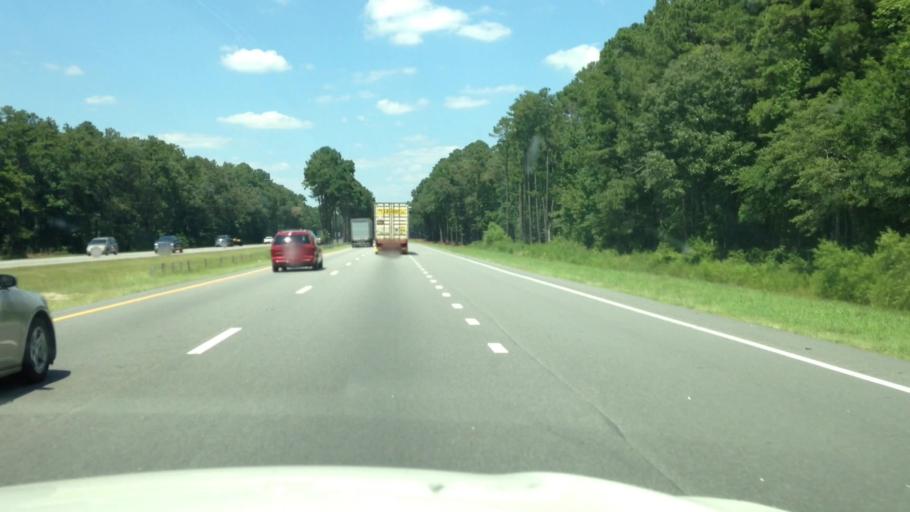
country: US
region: North Carolina
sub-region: Robeson County
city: Lumberton
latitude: 34.6769
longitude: -79.0037
